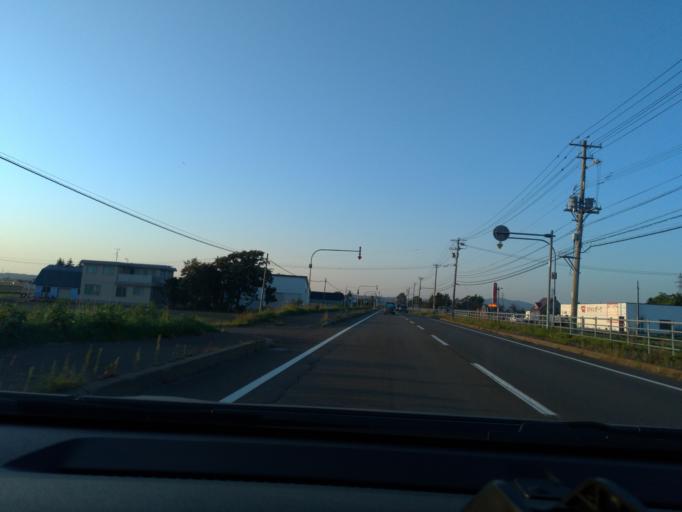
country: JP
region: Hokkaido
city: Tobetsu
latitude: 43.1947
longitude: 141.5236
